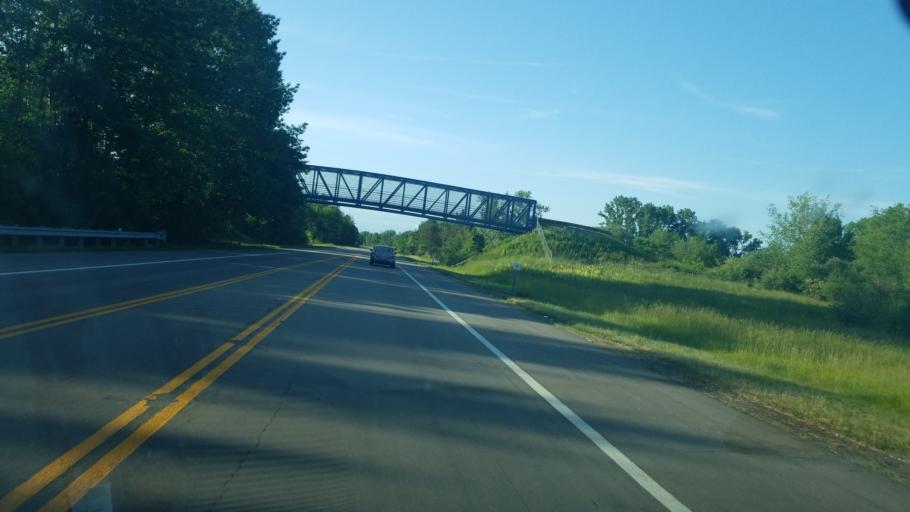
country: US
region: Ohio
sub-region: Portage County
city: Kent
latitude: 41.1402
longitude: -81.3204
